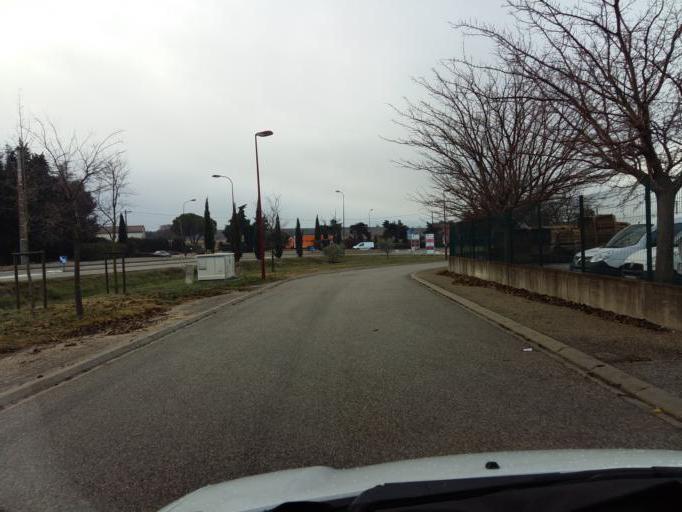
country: FR
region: Provence-Alpes-Cote d'Azur
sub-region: Departement du Vaucluse
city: Sablet
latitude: 44.1944
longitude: 4.9972
